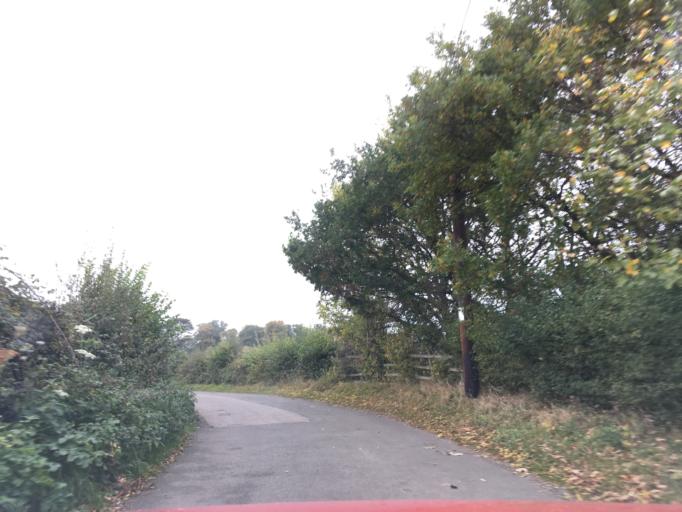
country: GB
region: England
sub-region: Gloucestershire
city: Stonehouse
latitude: 51.7537
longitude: -2.3065
